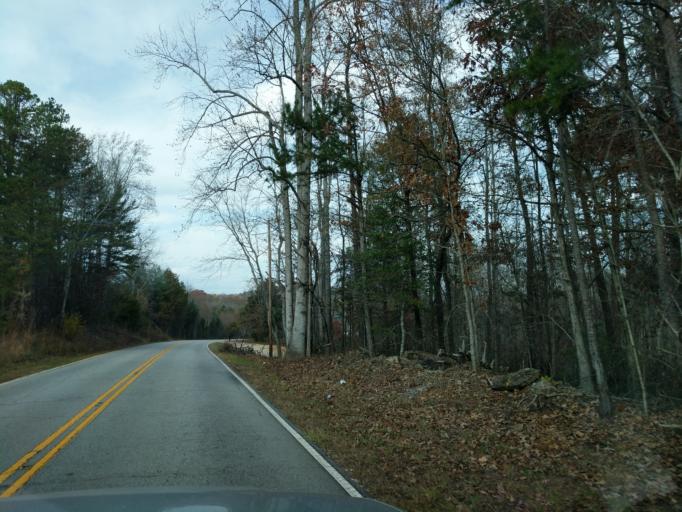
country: US
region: South Carolina
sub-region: Pickens County
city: Pickens
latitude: 34.8367
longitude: -82.8081
